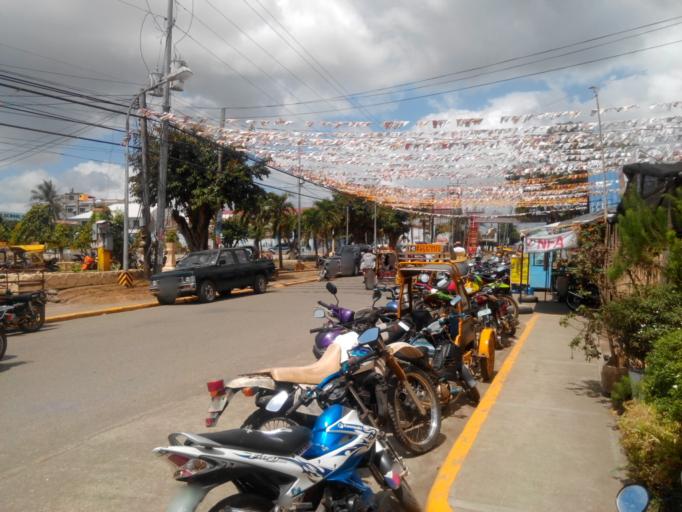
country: PH
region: Western Visayas
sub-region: Province of Iloilo
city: Passi
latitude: 11.1053
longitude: 122.6420
